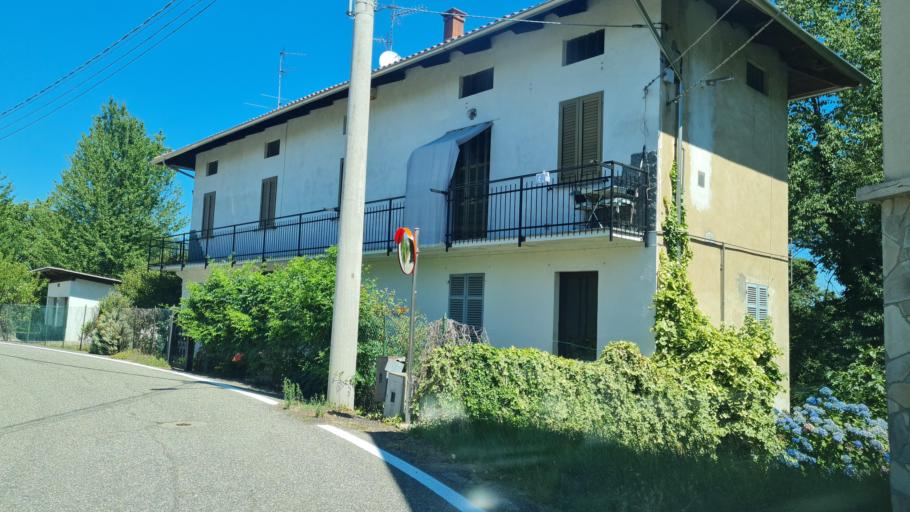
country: IT
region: Piedmont
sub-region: Provincia di Biella
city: Lessona
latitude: 45.5967
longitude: 8.1962
